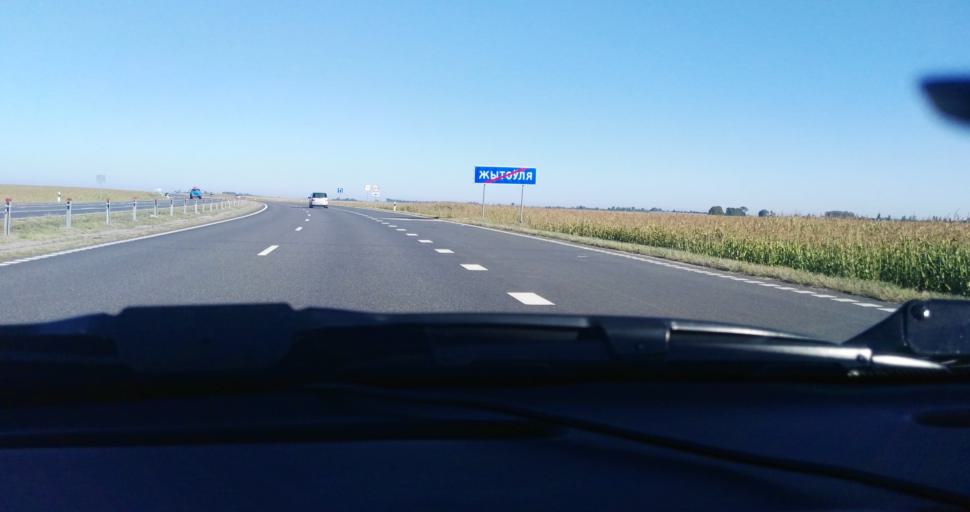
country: BY
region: Gomel
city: Buda-Kashalyova
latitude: 52.5209
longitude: 30.6258
